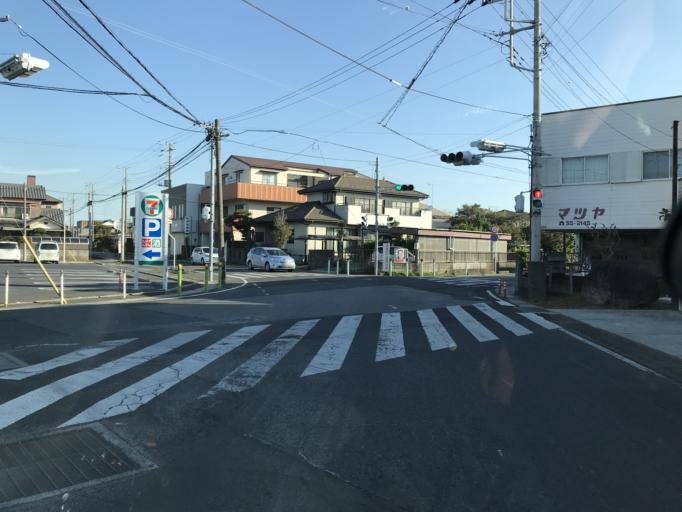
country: JP
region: Chiba
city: Asahi
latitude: 35.7265
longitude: 140.6855
